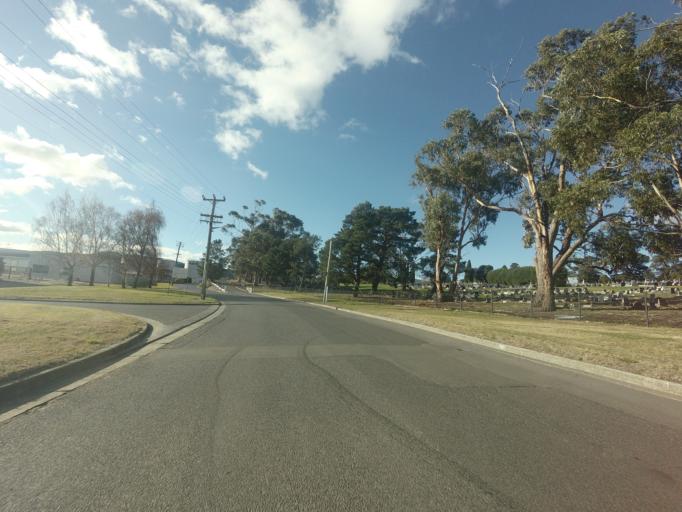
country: AU
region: Tasmania
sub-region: Hobart
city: New Town
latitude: -42.8486
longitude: 147.3192
